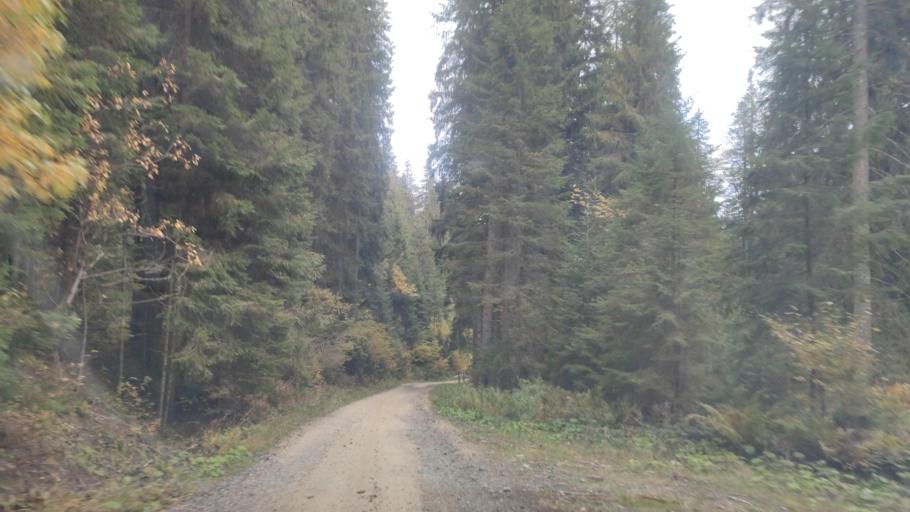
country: RO
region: Harghita
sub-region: Comuna Madaras
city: Madaras
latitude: 46.4715
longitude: 25.6321
